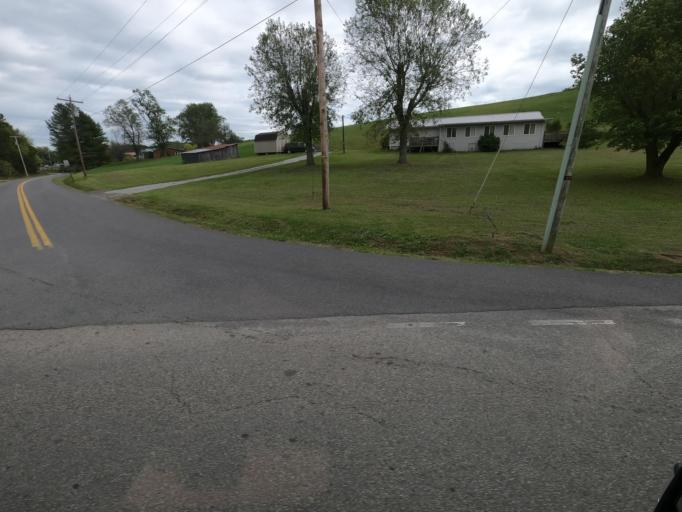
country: US
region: Tennessee
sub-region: Washington County
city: Jonesborough
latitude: 36.2245
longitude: -82.5662
